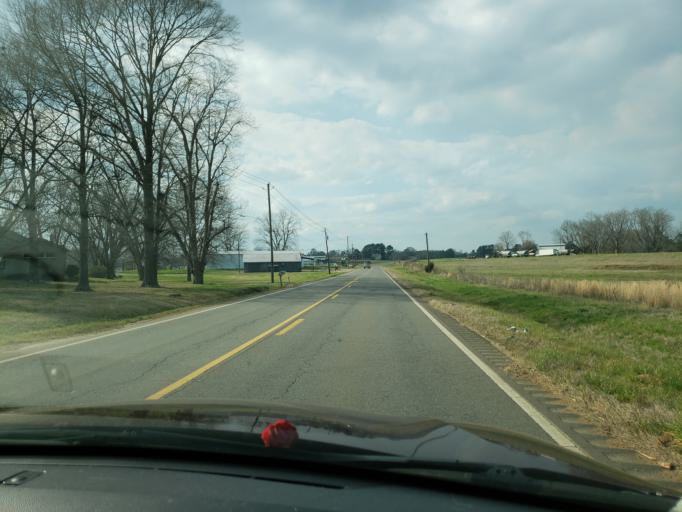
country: US
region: Alabama
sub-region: Hale County
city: Greensboro
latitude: 32.7143
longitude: -87.6162
